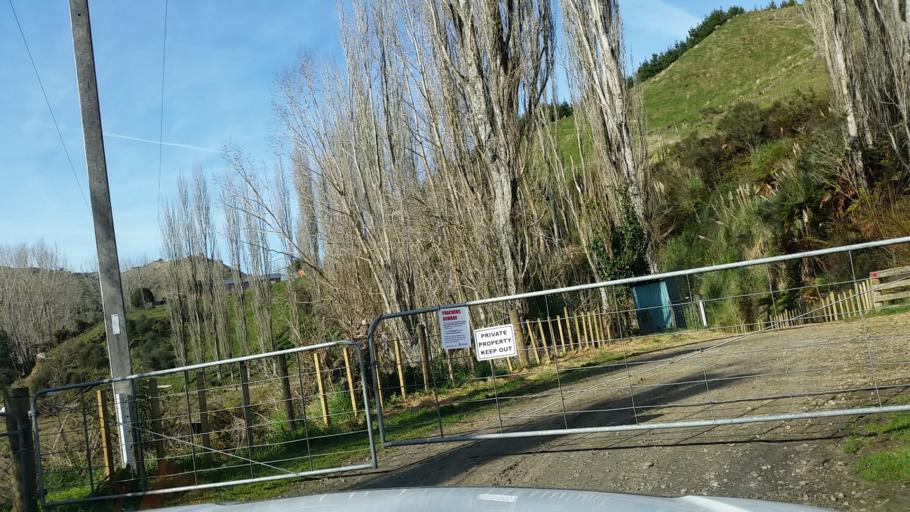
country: NZ
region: Taranaki
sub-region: South Taranaki District
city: Eltham
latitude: -39.3659
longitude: 174.5186
